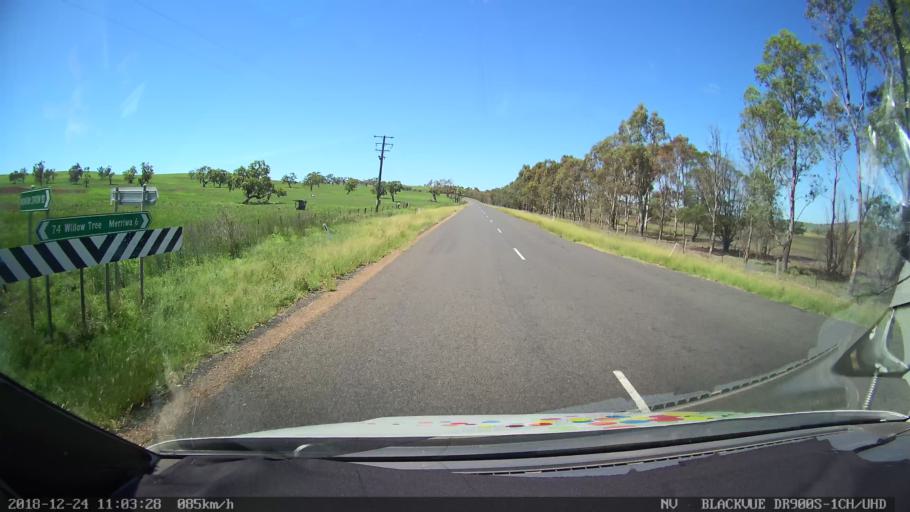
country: AU
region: New South Wales
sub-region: Upper Hunter Shire
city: Merriwa
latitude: -32.0970
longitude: 150.3688
